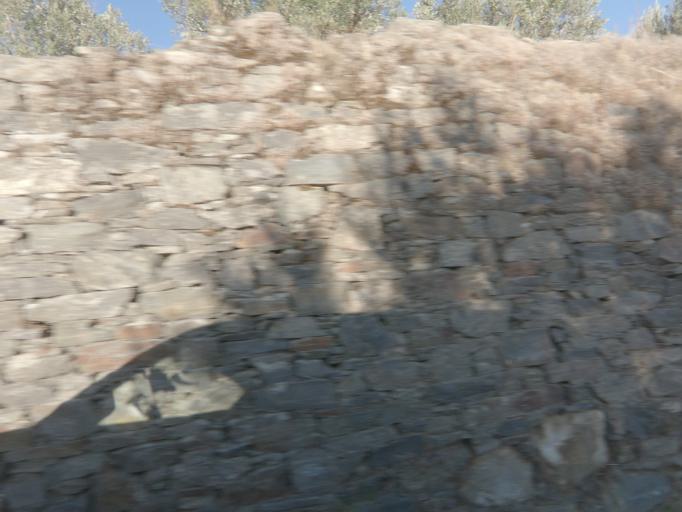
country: PT
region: Vila Real
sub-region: Peso da Regua
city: Godim
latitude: 41.1629
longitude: -7.8253
